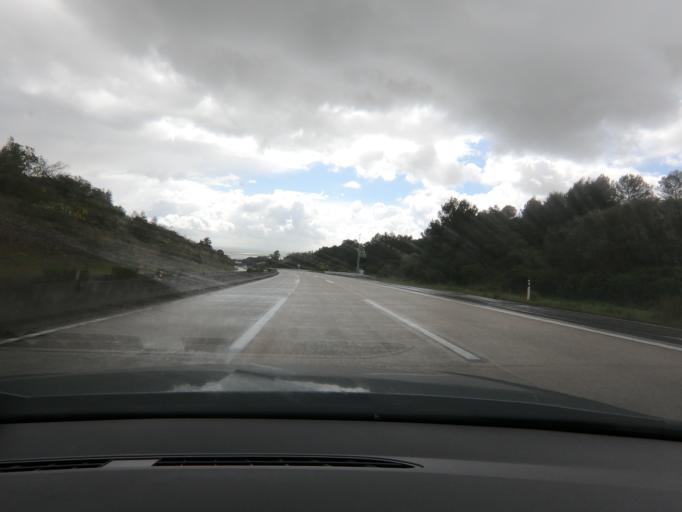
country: PT
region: Lisbon
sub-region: Vila Franca de Xira
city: Vialonga
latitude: 38.9075
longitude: -9.0648
